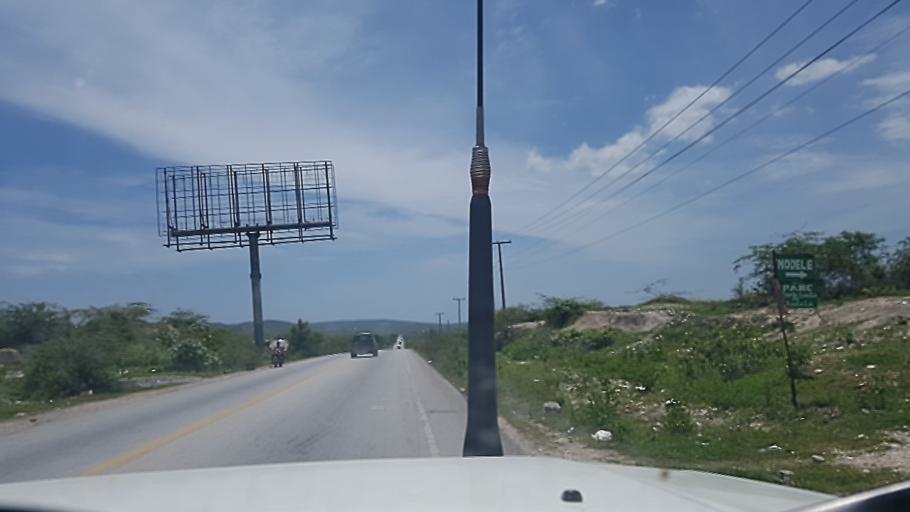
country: HT
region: Artibonite
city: Saint-Marc
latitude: 19.1521
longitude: -72.6339
